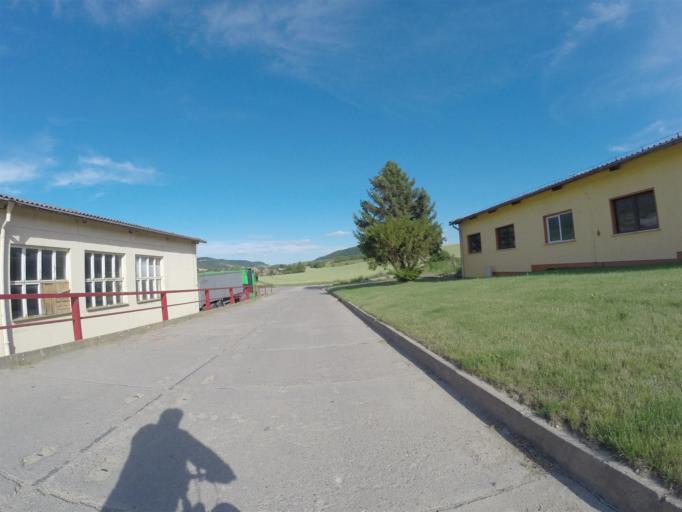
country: DE
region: Thuringia
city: Golmsdorf
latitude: 50.9703
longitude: 11.6714
